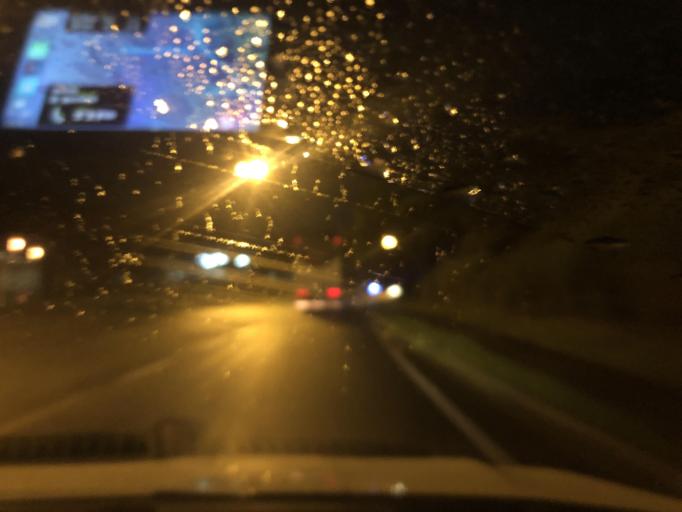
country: BR
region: Santa Catarina
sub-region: Joinville
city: Joinville
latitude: -26.3833
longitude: -48.8452
